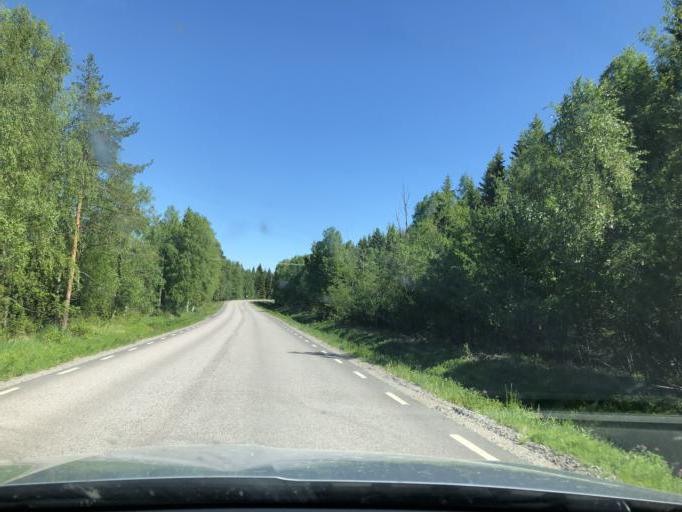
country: SE
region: Norrbotten
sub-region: Lulea Kommun
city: Gammelstad
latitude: 65.6513
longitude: 22.0323
